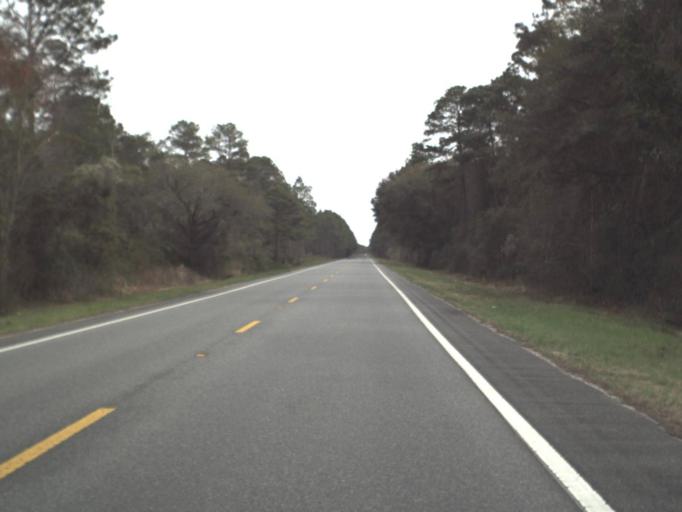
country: US
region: Florida
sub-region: Gadsden County
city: Midway
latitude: 30.3369
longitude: -84.4834
